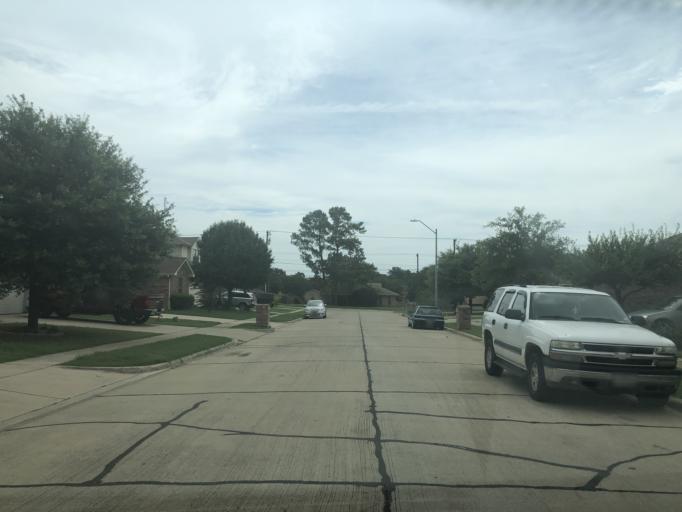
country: US
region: Texas
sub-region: Dallas County
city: Irving
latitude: 32.7952
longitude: -96.9781
